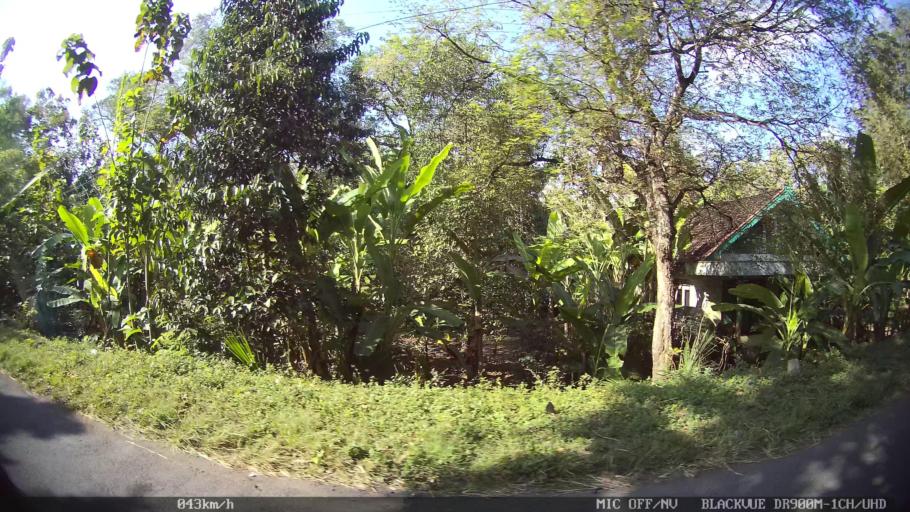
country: ID
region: Daerah Istimewa Yogyakarta
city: Kasihan
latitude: -7.8363
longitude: 110.2807
